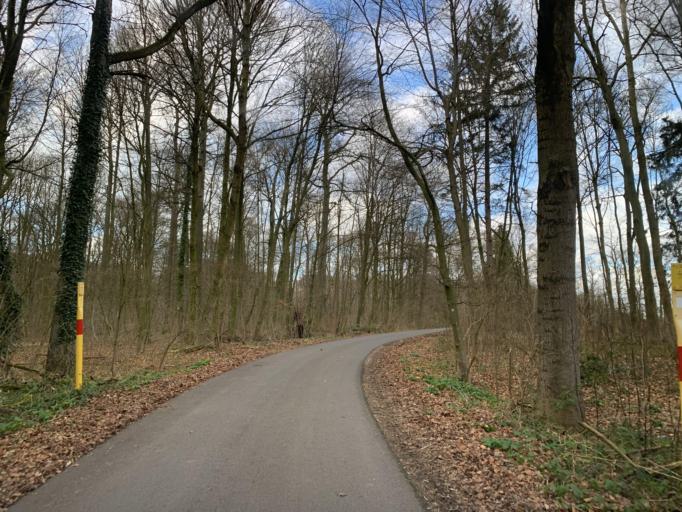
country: DE
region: North Rhine-Westphalia
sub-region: Regierungsbezirk Munster
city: Horstmar
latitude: 52.0906
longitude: 7.3129
